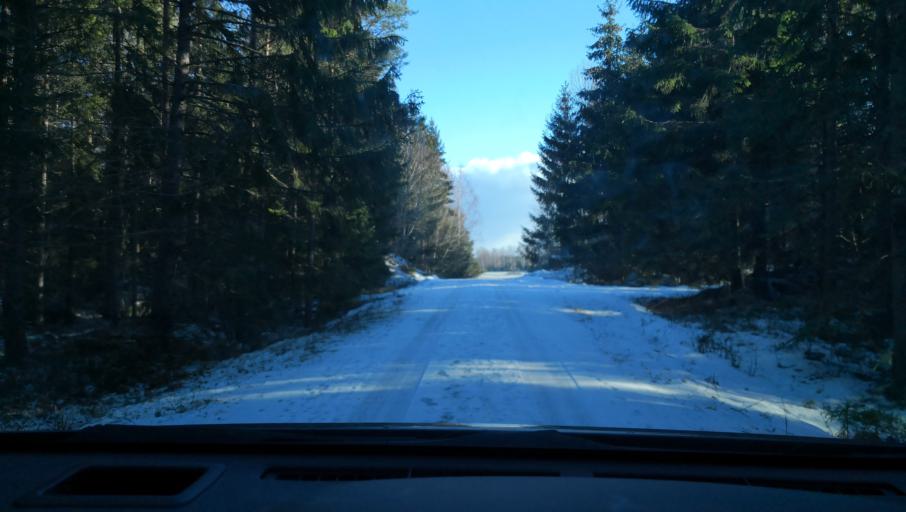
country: SE
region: Uppsala
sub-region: Enkopings Kommun
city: Hummelsta
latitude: 59.6248
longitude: 16.9310
